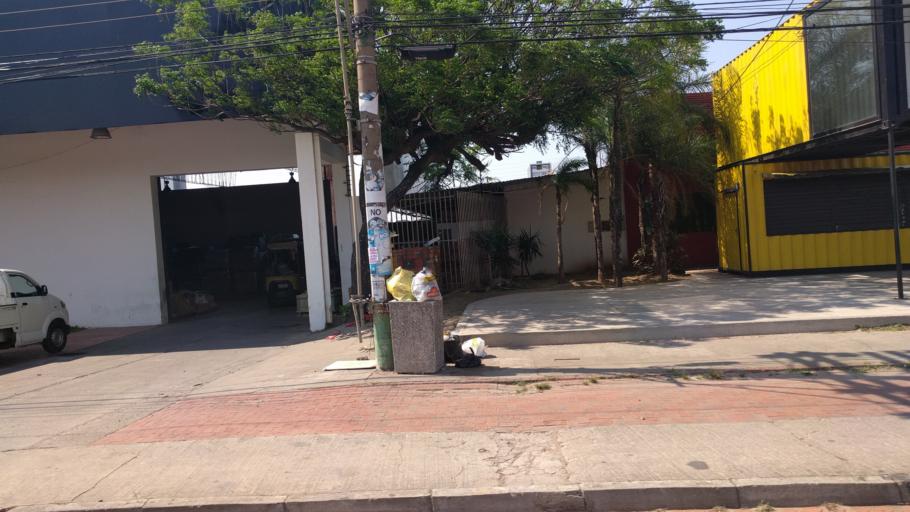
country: BO
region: Santa Cruz
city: Santa Cruz de la Sierra
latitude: -17.7610
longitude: -63.1795
